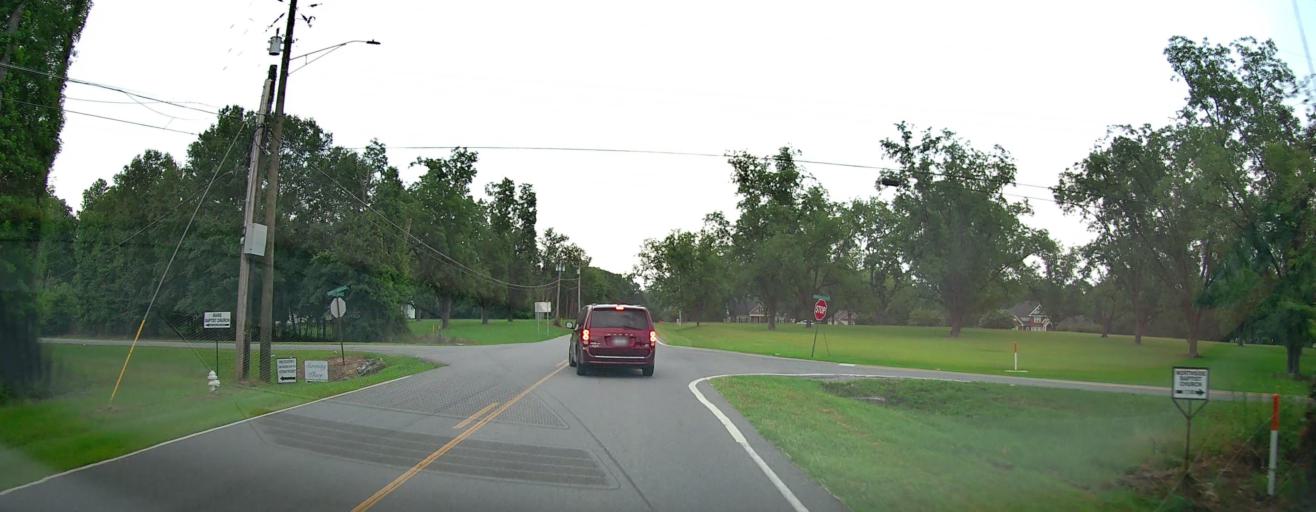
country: US
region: Georgia
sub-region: Laurens County
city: Dublin
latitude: 32.5708
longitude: -82.9094
